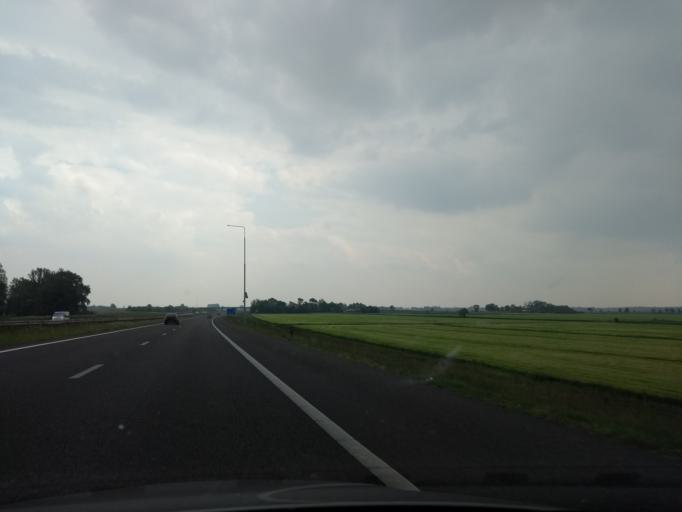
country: NL
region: Friesland
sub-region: Gemeente Skarsterlan
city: Joure
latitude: 52.9696
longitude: 5.7618
